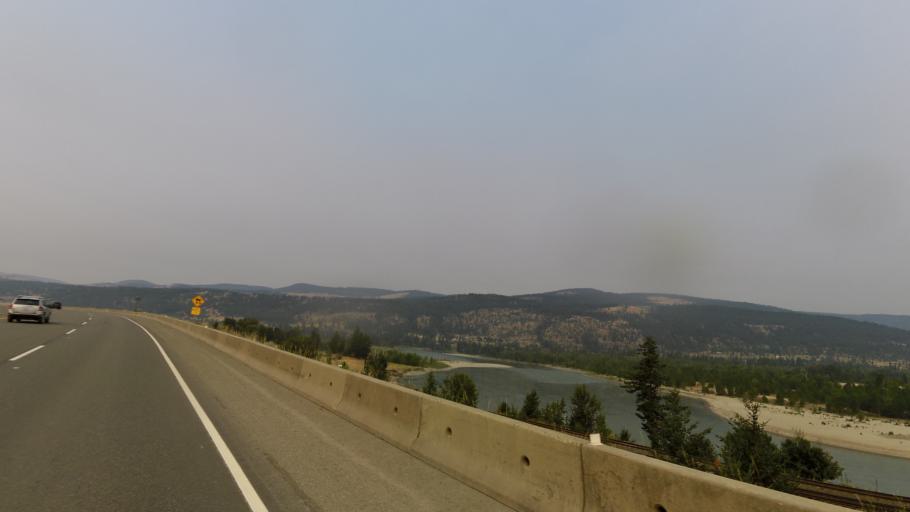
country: CA
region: British Columbia
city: Kamloops
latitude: 50.8609
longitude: -120.2690
